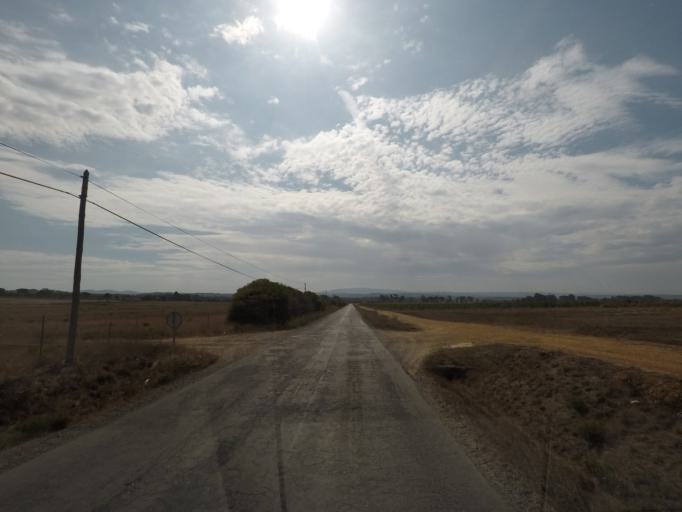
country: PT
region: Beja
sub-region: Odemira
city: Sao Teotonio
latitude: 37.4715
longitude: -8.7555
